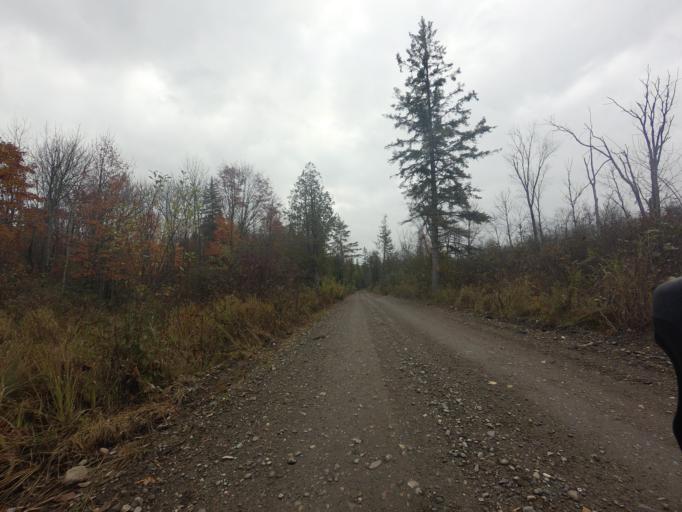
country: CA
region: Ontario
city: Renfrew
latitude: 45.1731
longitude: -76.6812
